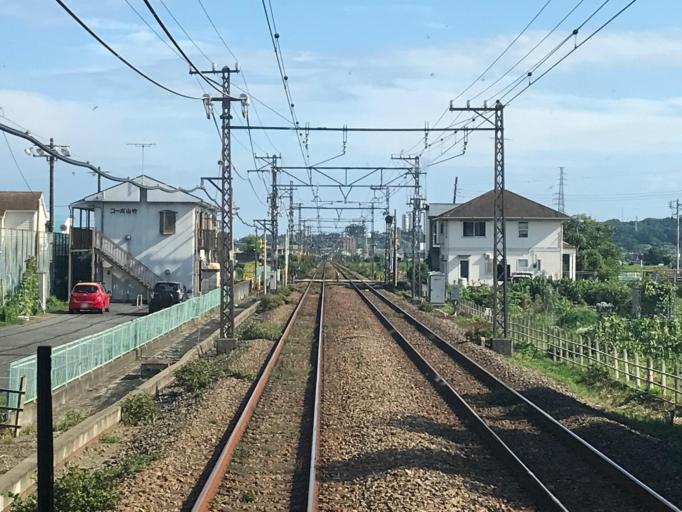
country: JP
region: Kanagawa
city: Odawara
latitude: 35.3111
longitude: 139.1424
